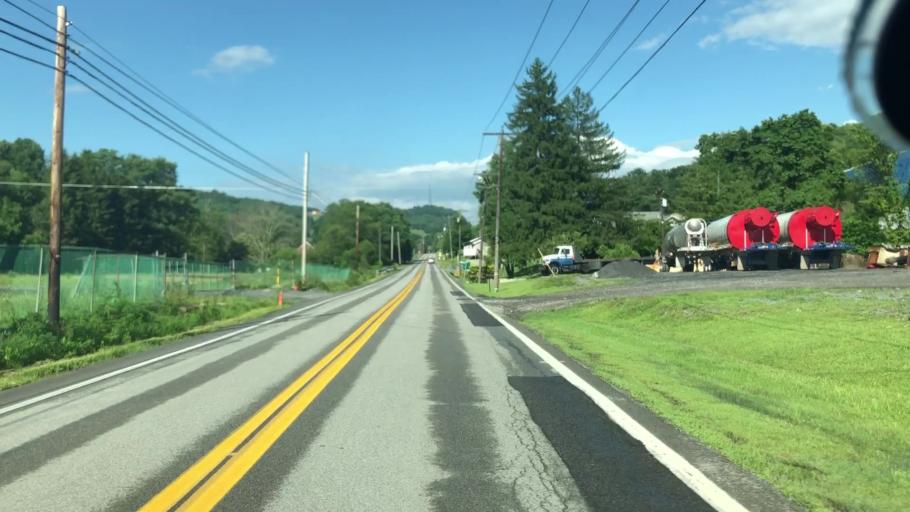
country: US
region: West Virginia
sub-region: Harrison County
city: Bridgeport
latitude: 39.2987
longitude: -80.1983
